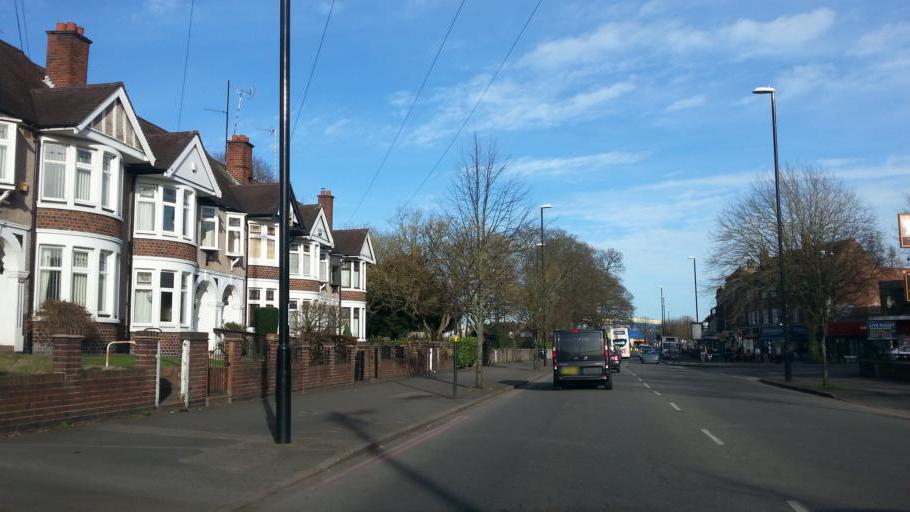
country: GB
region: England
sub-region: Coventry
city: Coventry
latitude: 52.4112
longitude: -1.4759
